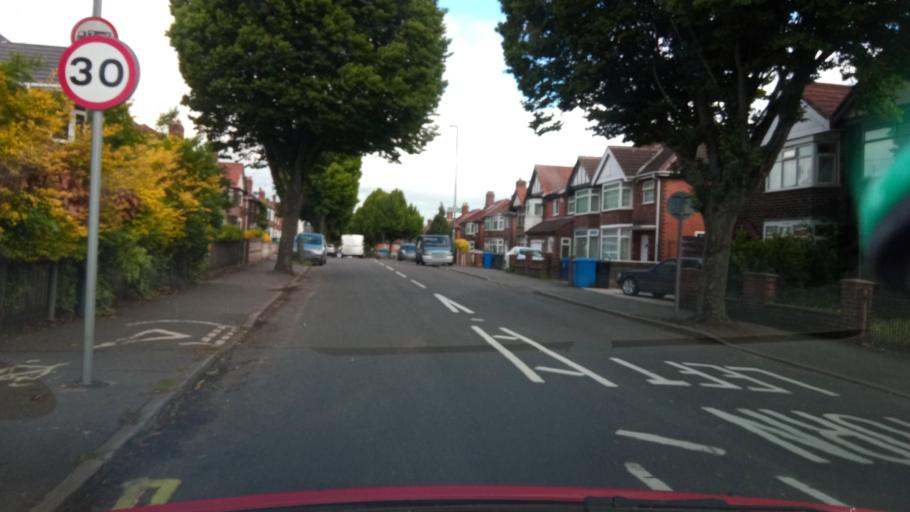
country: GB
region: England
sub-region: Derby
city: Derby
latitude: 52.8974
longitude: -1.4740
